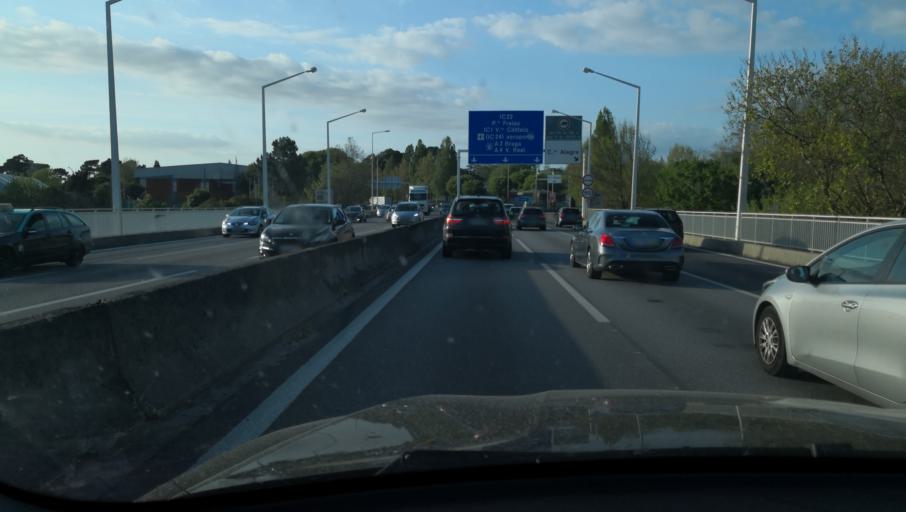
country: PT
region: Porto
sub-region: Vila Nova de Gaia
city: Canidelo
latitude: 41.1490
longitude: -8.6407
